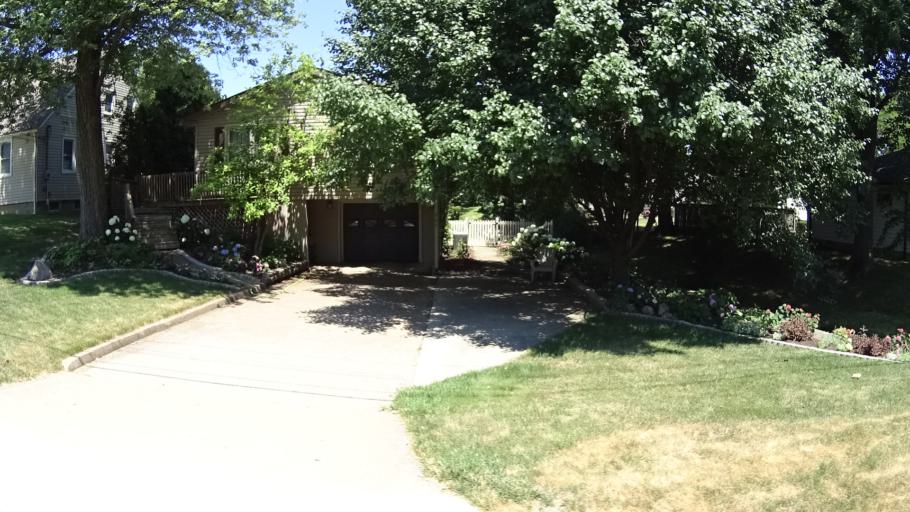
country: US
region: Ohio
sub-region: Erie County
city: Huron
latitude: 41.3910
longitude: -82.5621
